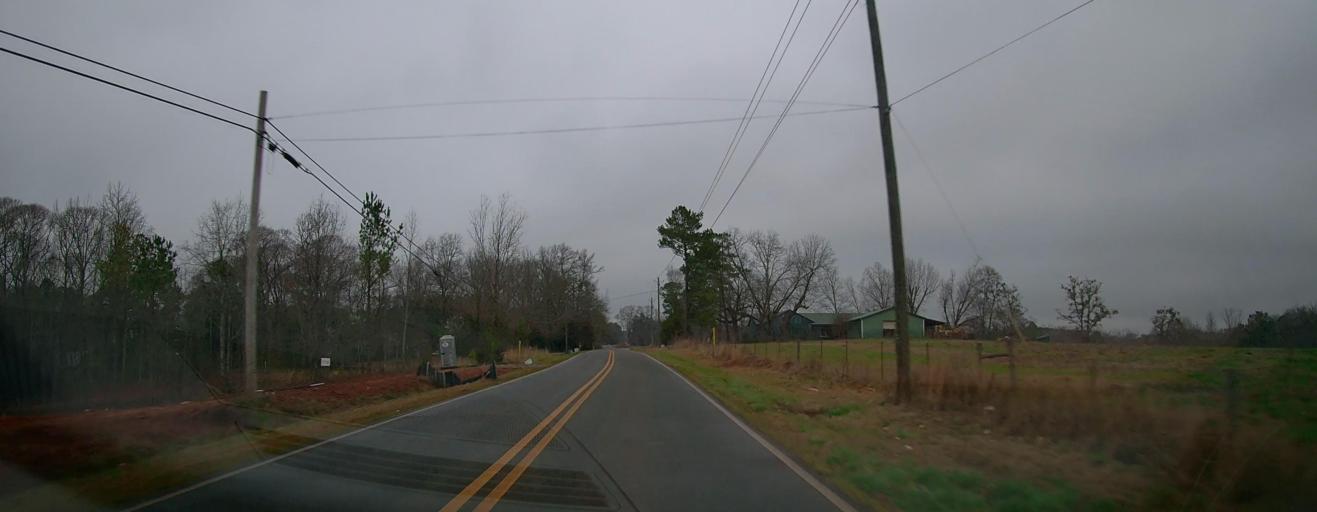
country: US
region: Georgia
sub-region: Pike County
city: Zebulon
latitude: 33.1298
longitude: -84.3457
